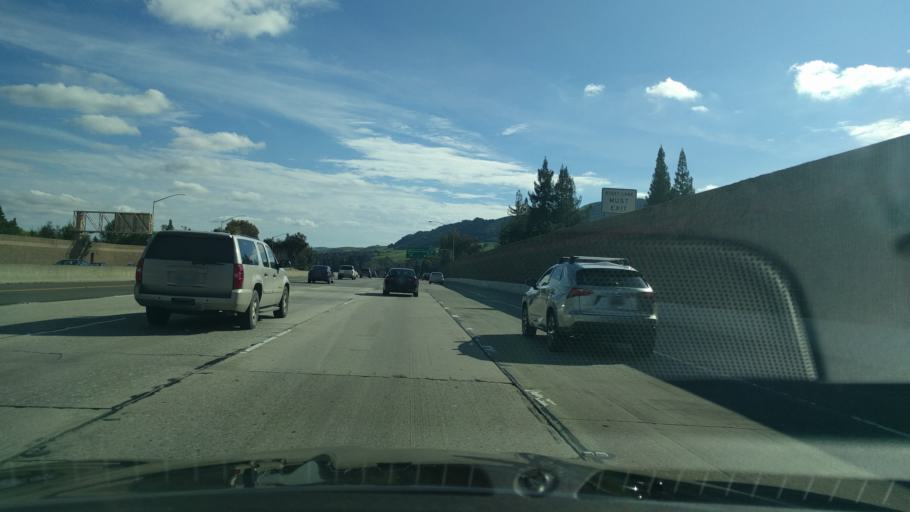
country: US
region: California
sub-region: Contra Costa County
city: Danville
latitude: 37.8171
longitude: -121.9935
